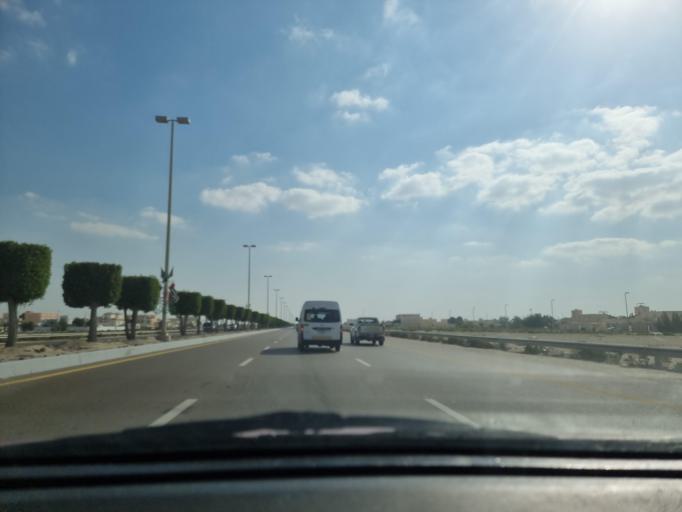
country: AE
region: Abu Dhabi
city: Abu Dhabi
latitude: 24.3998
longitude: 54.7172
